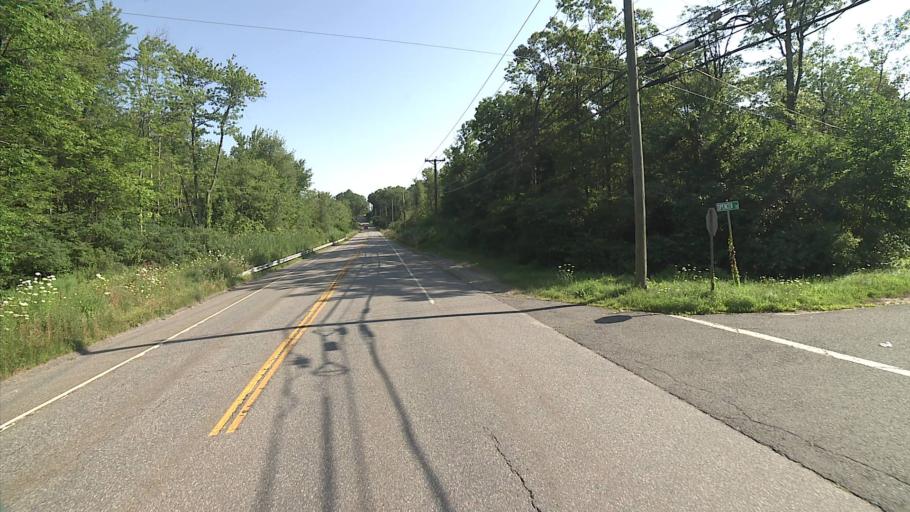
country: US
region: Connecticut
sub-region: Litchfield County
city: Torrington
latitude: 41.8406
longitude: -73.0757
